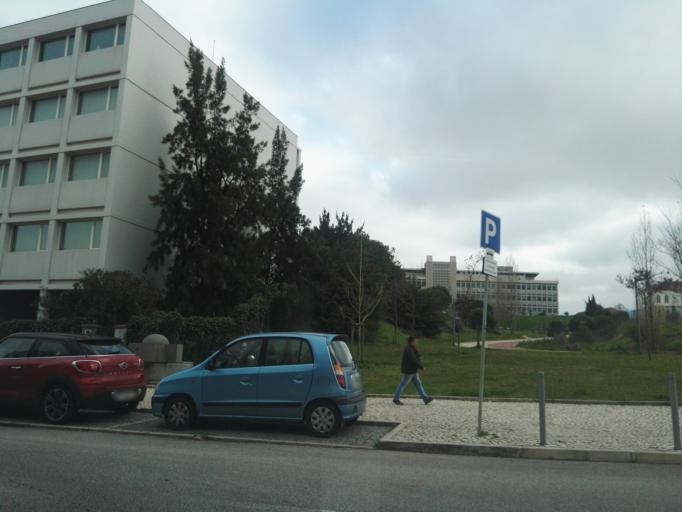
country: PT
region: Lisbon
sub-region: Lisbon
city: Lisbon
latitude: 38.7351
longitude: -9.1601
